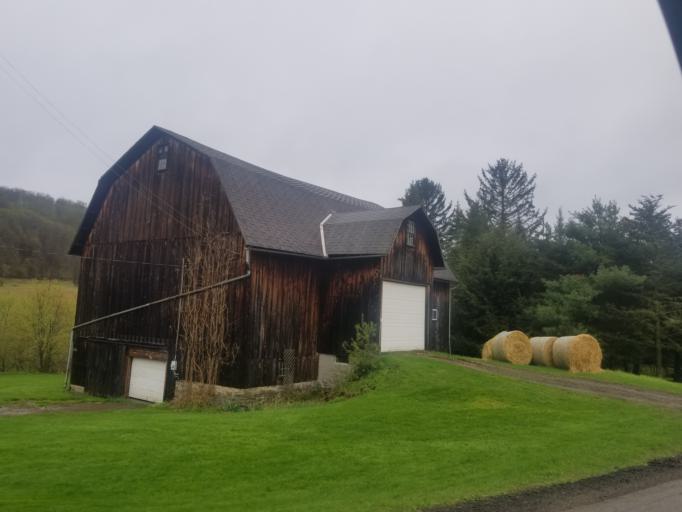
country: US
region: New York
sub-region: Allegany County
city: Andover
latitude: 41.9939
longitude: -77.8012
